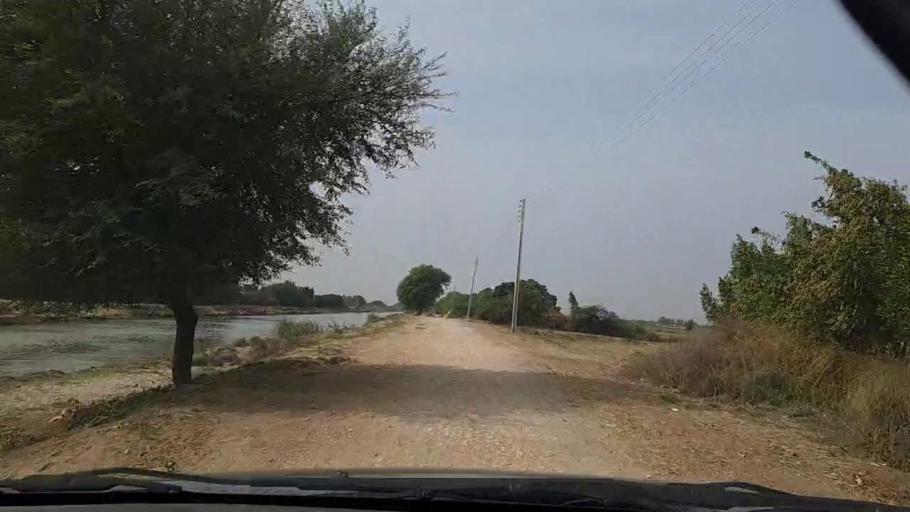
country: PK
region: Sindh
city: Thatta
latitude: 24.5700
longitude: 67.8584
